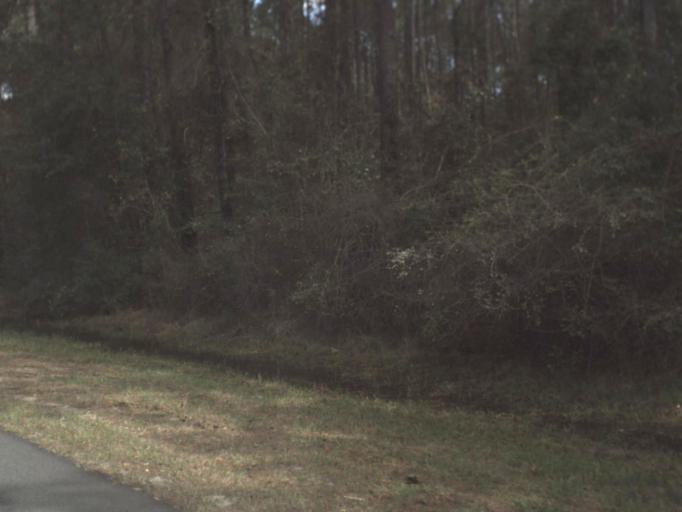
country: US
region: Florida
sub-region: Leon County
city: Woodville
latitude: 30.2974
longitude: -84.3492
